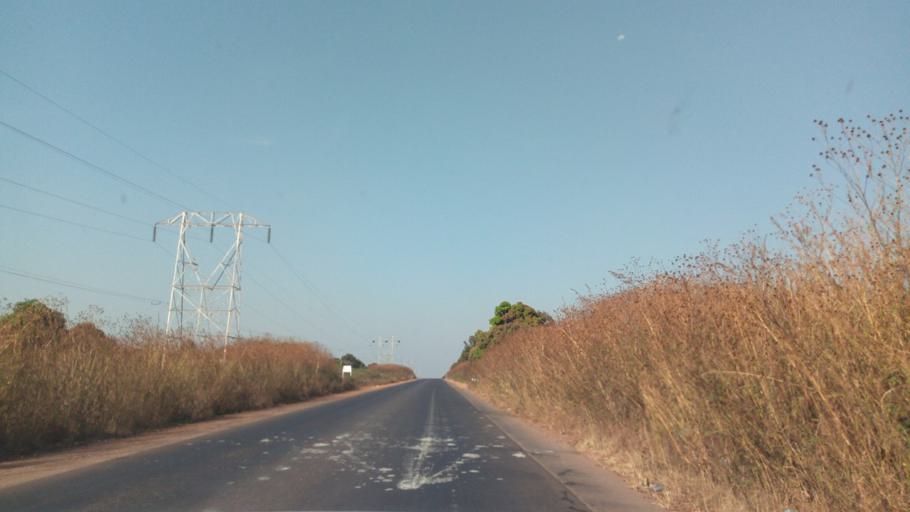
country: CD
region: Katanga
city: Likasi
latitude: -11.0012
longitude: 26.8735
